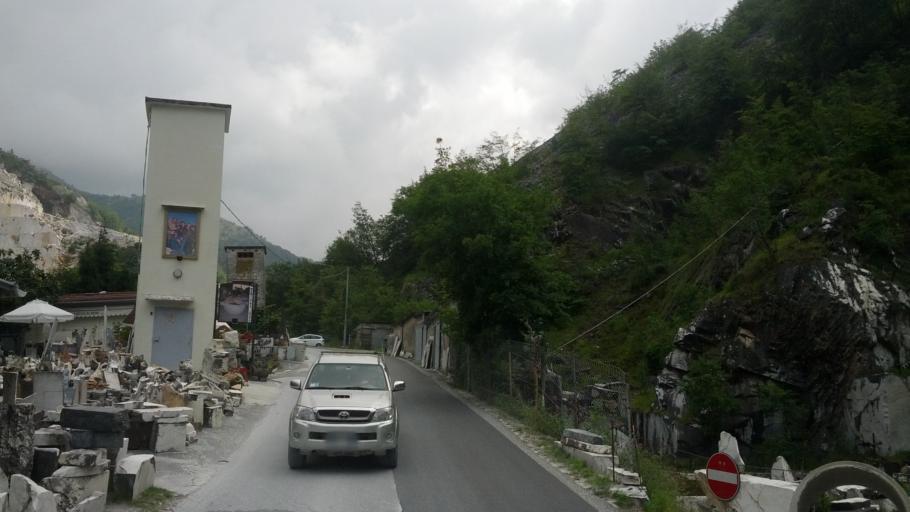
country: IT
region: Tuscany
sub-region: Provincia di Massa-Carrara
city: Montignoso
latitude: 44.0807
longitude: 10.1432
